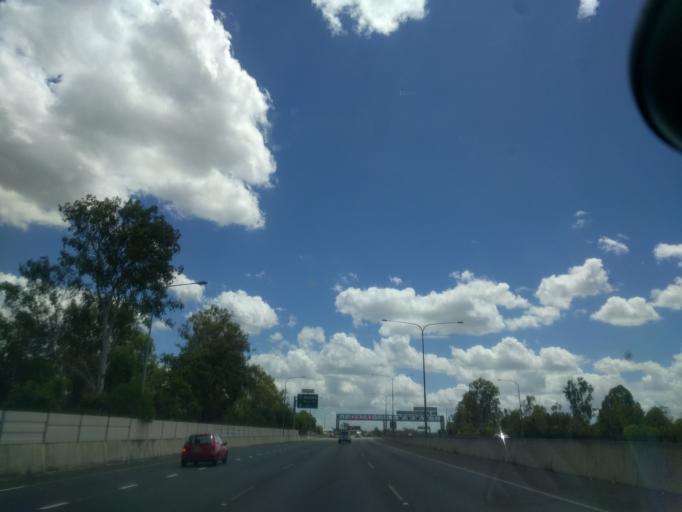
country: AU
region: Queensland
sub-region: Brisbane
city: Wacol
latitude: -27.5970
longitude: 152.9216
